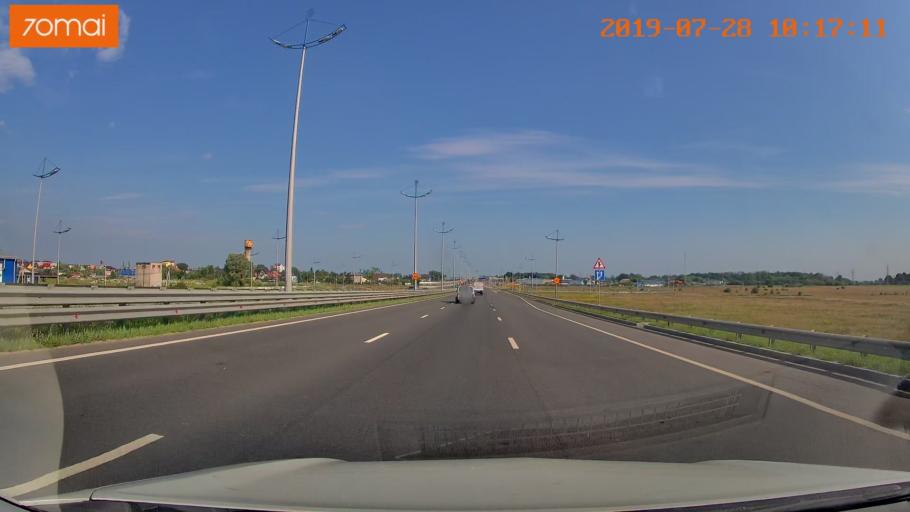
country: RU
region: Kaliningrad
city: Maloye Isakovo
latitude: 54.7366
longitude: 20.5959
